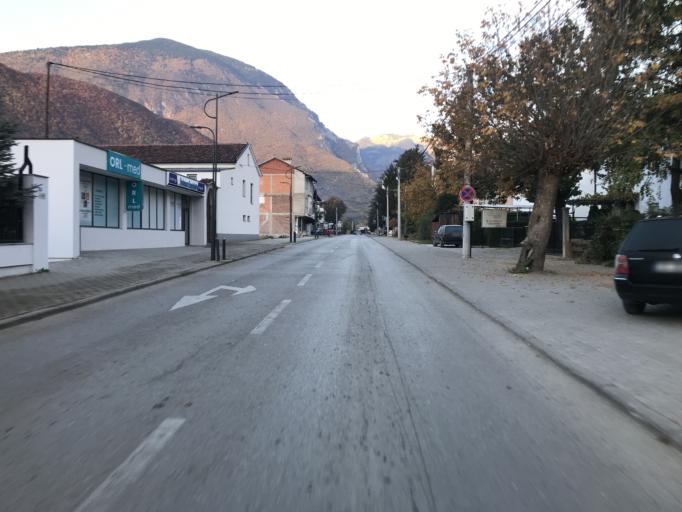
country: XK
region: Pec
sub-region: Komuna e Pejes
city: Peje
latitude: 42.6614
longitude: 20.2781
